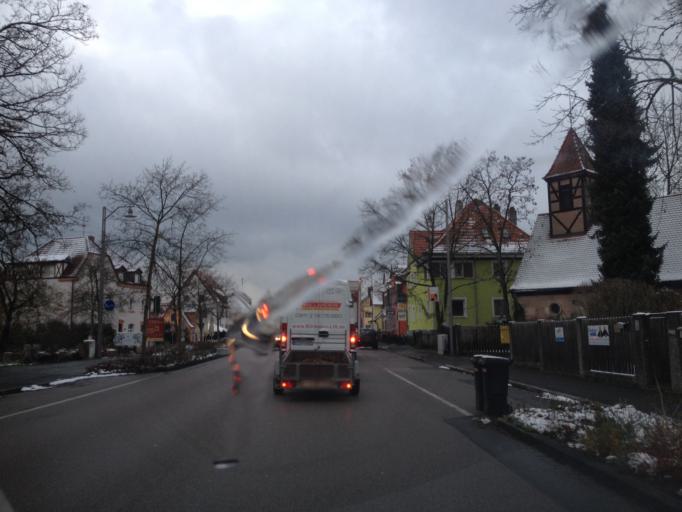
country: DE
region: Bavaria
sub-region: Regierungsbezirk Mittelfranken
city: Schwaig
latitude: 49.4821
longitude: 11.2029
